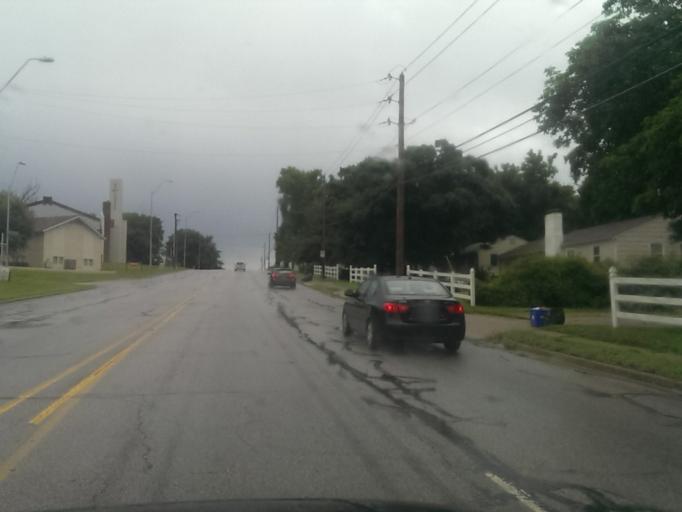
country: US
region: Kansas
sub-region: Johnson County
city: Leawood
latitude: 38.9498
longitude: -94.5823
